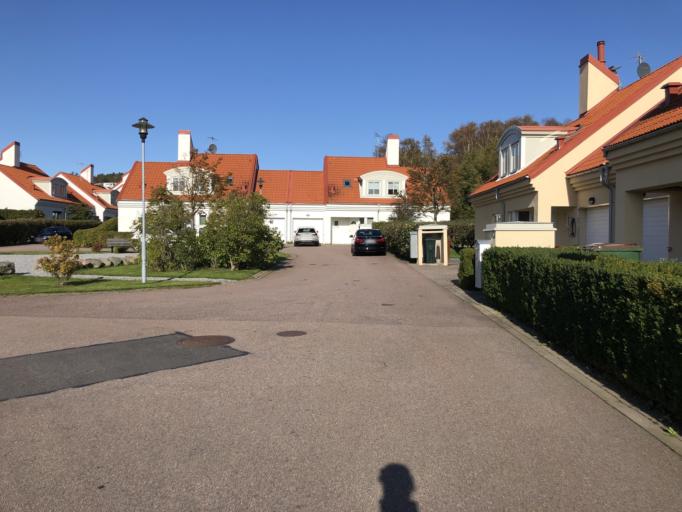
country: SE
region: Vaestra Goetaland
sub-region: Goteborg
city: Billdal
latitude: 57.6187
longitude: 11.8870
